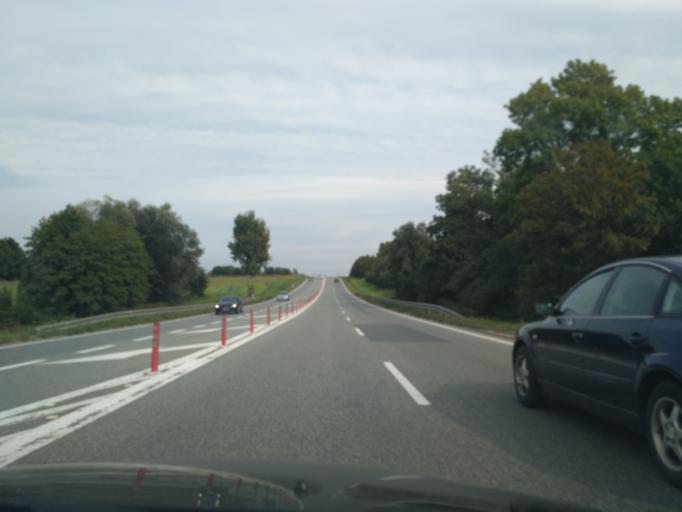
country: PL
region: Subcarpathian Voivodeship
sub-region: Powiat rzeszowski
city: Swilcza
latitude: 50.0715
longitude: 21.8710
